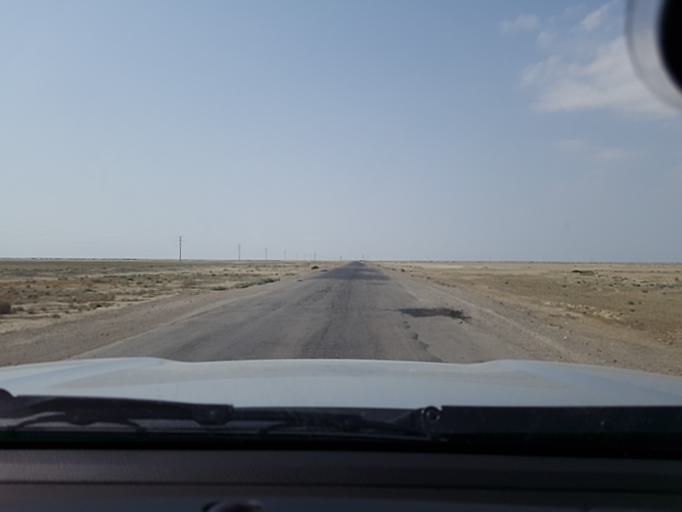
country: TM
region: Balkan
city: Gumdag
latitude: 39.0175
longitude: 54.5850
